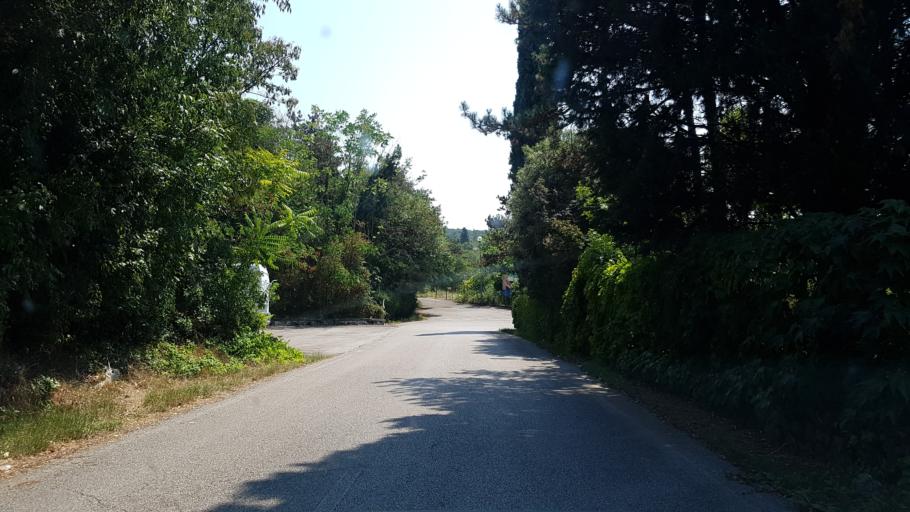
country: IT
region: Friuli Venezia Giulia
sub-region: Provincia di Gorizia
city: Sagrado
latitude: 45.8757
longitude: 13.4900
